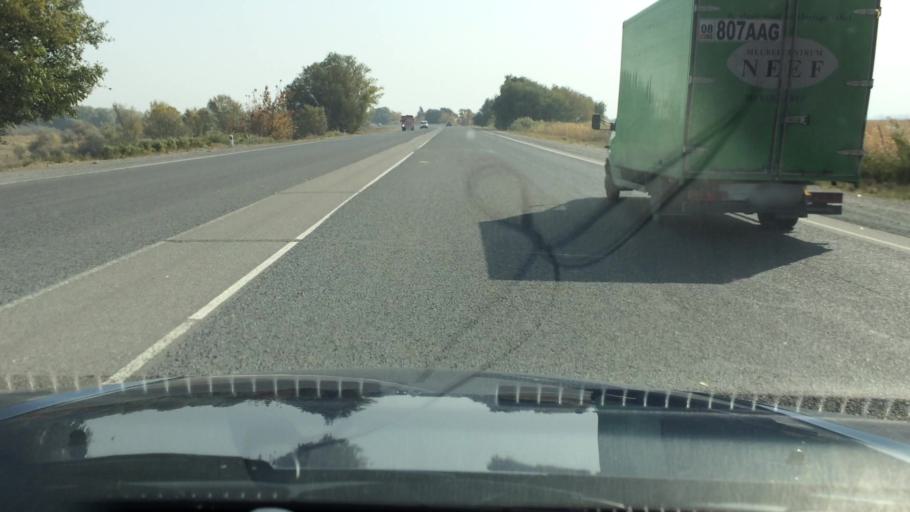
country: KG
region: Chuy
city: Kant
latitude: 42.9425
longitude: 74.9658
